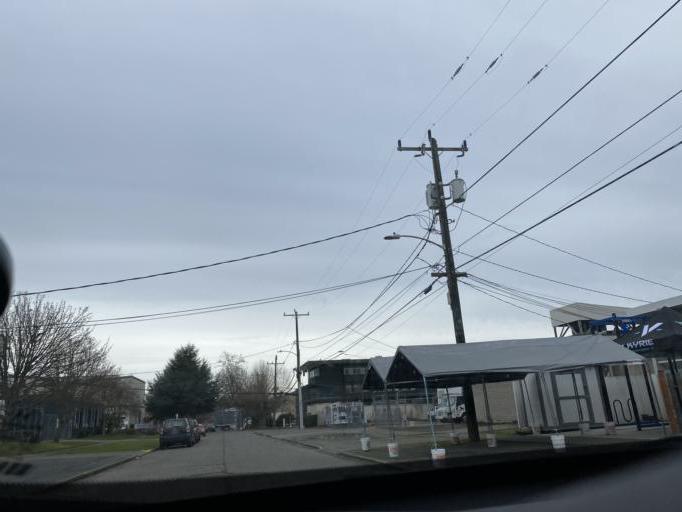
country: US
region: Washington
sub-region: King County
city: Seattle
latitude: 47.6568
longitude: -122.3859
